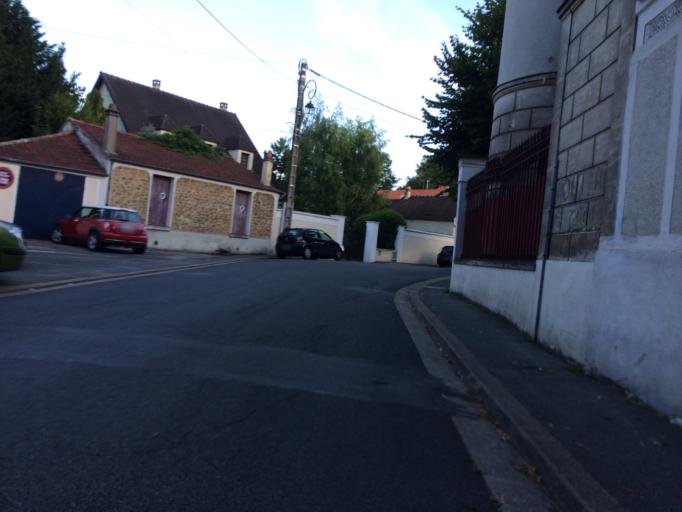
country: FR
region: Ile-de-France
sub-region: Departement de l'Essonne
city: Draveil
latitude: 48.6868
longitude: 2.4319
